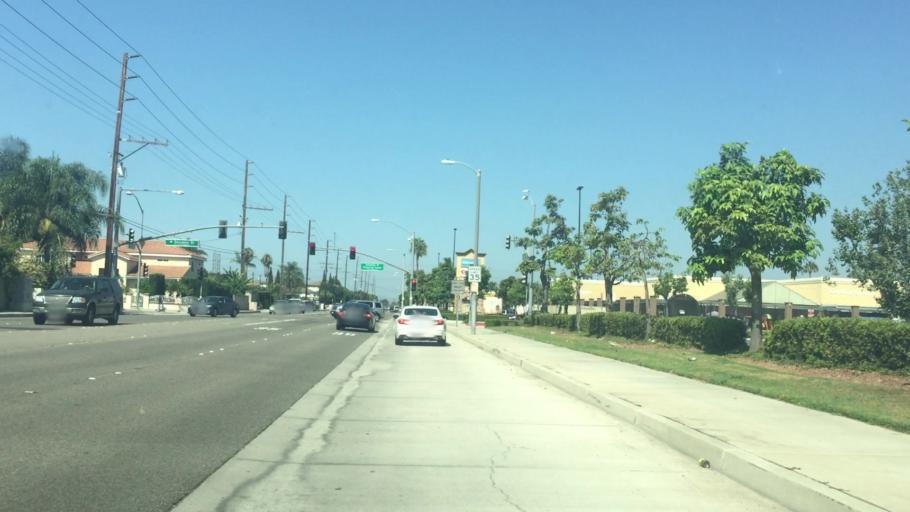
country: US
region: California
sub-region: Orange County
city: Westminster
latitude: 33.7667
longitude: -117.9918
